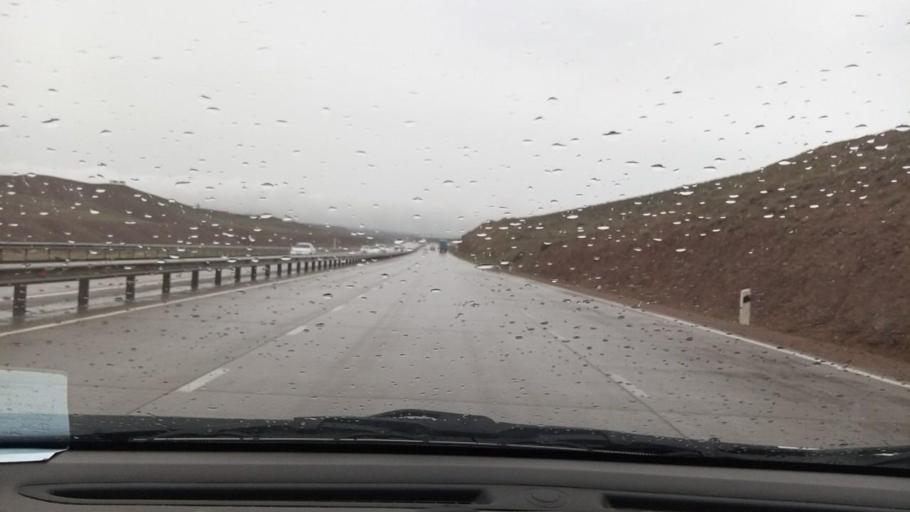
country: UZ
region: Namangan
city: Pop Shahri
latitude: 40.9297
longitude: 70.7084
